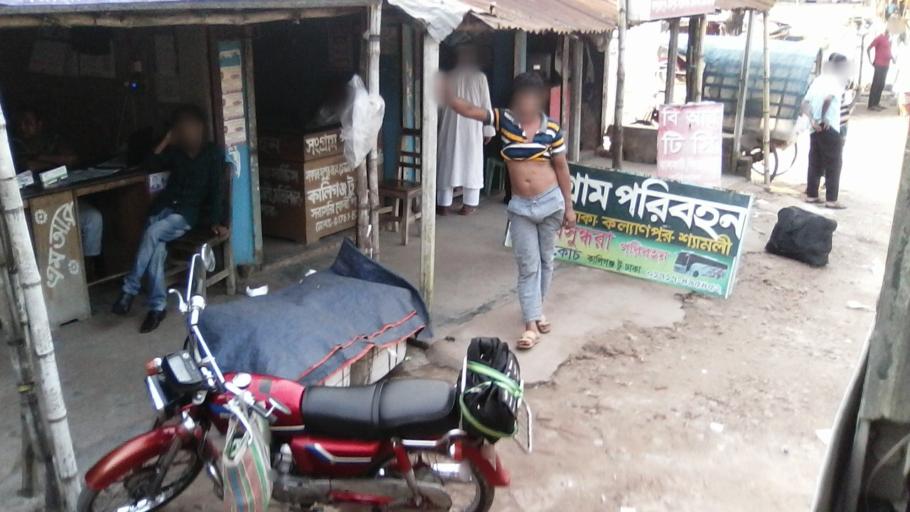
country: IN
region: West Bengal
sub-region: North 24 Parganas
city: Taki
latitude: 22.4611
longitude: 89.0329
